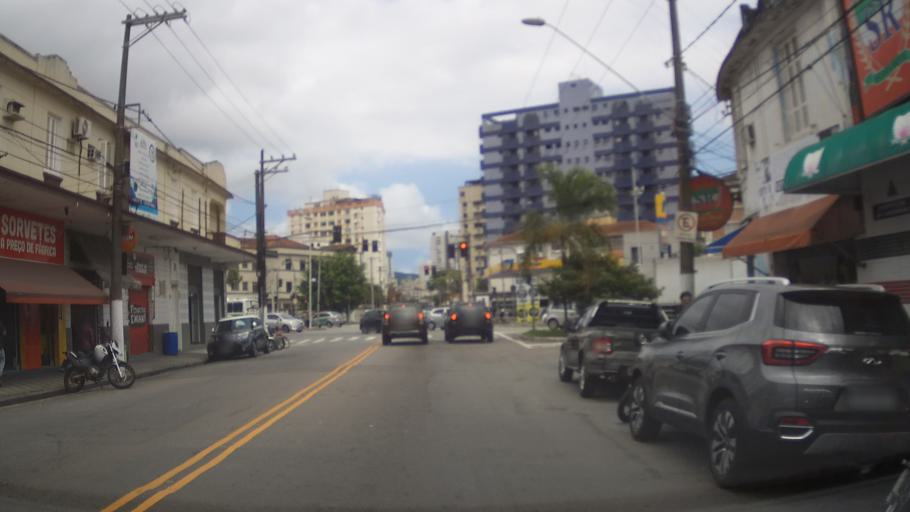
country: BR
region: Sao Paulo
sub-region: Santos
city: Santos
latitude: -23.9624
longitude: -46.3139
